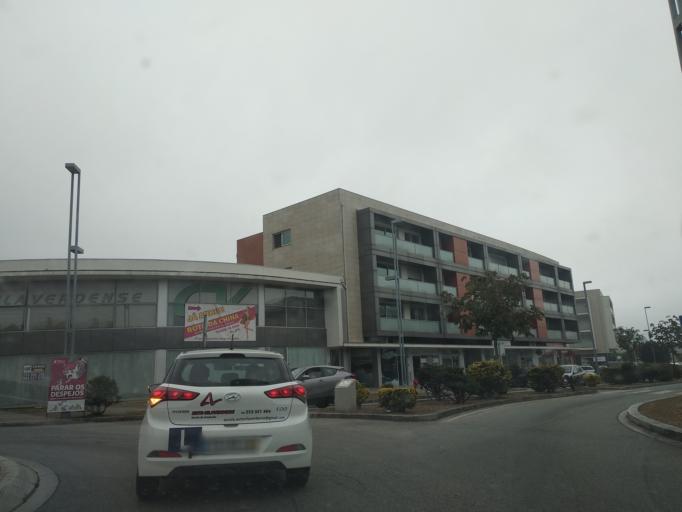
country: PT
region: Braga
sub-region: Vila Verde
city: Vila Verde
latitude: 41.6427
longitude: -8.4352
